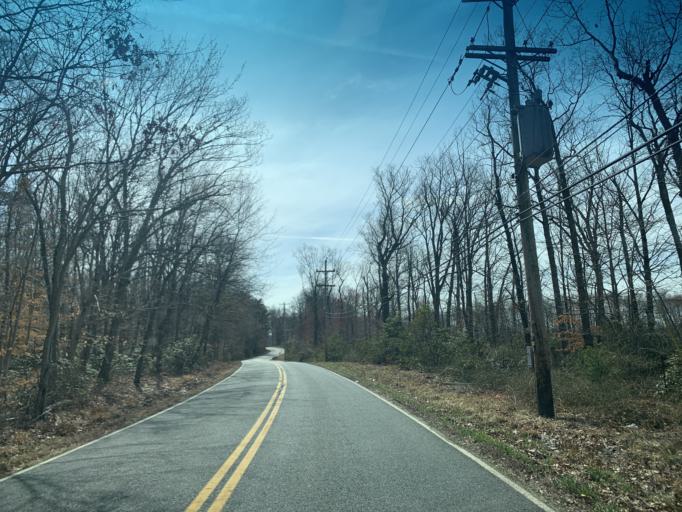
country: US
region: Maryland
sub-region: Cecil County
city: Charlestown
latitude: 39.5667
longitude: -76.0227
